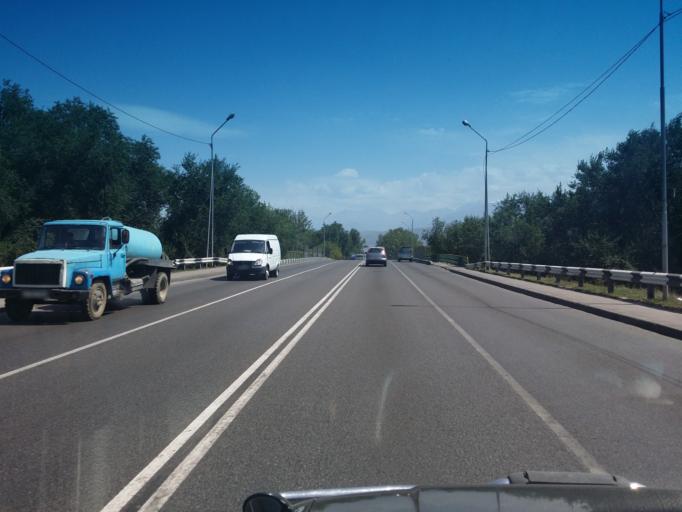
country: KZ
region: Almaty Oblysy
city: Pervomayskiy
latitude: 43.3428
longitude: 76.9768
